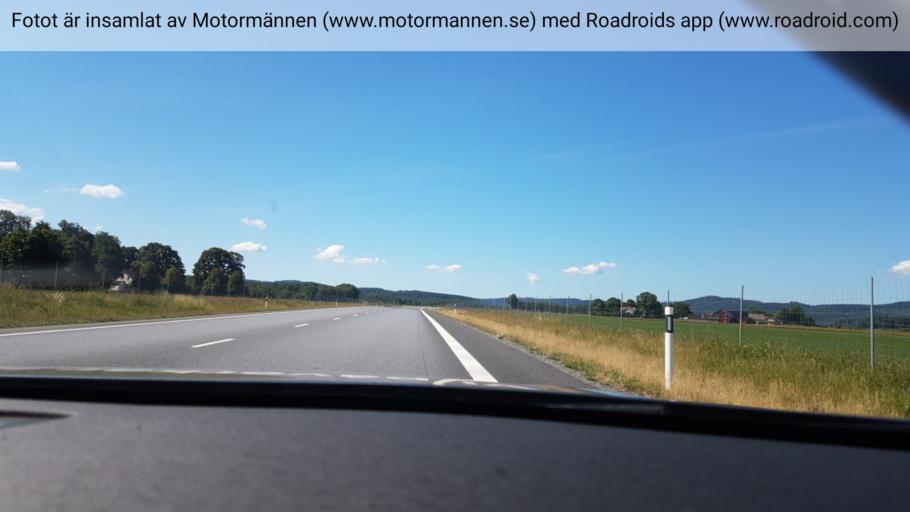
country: SE
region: Vaestra Goetaland
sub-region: Marks Kommun
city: Horred
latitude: 57.4471
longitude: 12.5676
